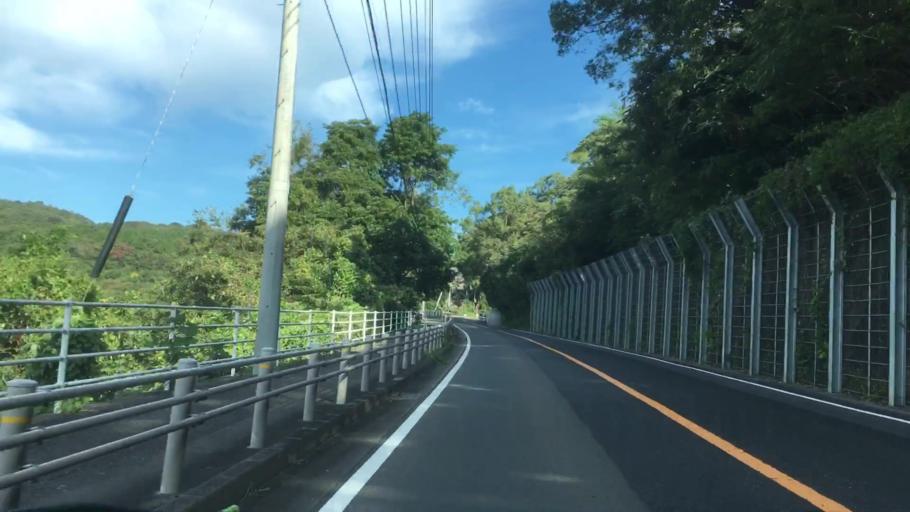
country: JP
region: Nagasaki
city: Sasebo
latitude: 33.0860
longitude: 129.7553
